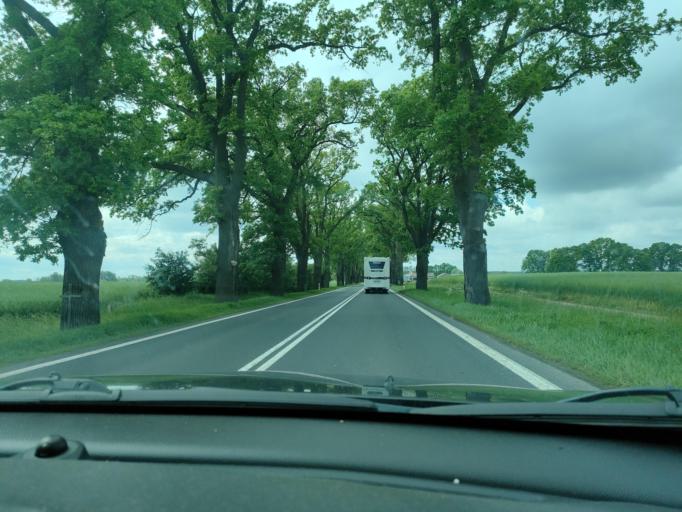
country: PL
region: Kujawsko-Pomorskie
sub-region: Powiat bydgoski
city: Osielsko
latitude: 53.2349
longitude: 18.1474
